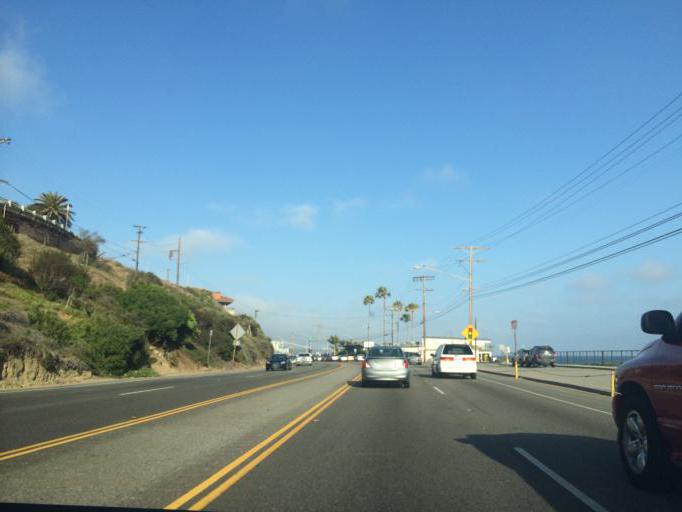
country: US
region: California
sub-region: Los Angeles County
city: Topanga
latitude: 34.0392
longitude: -118.5582
